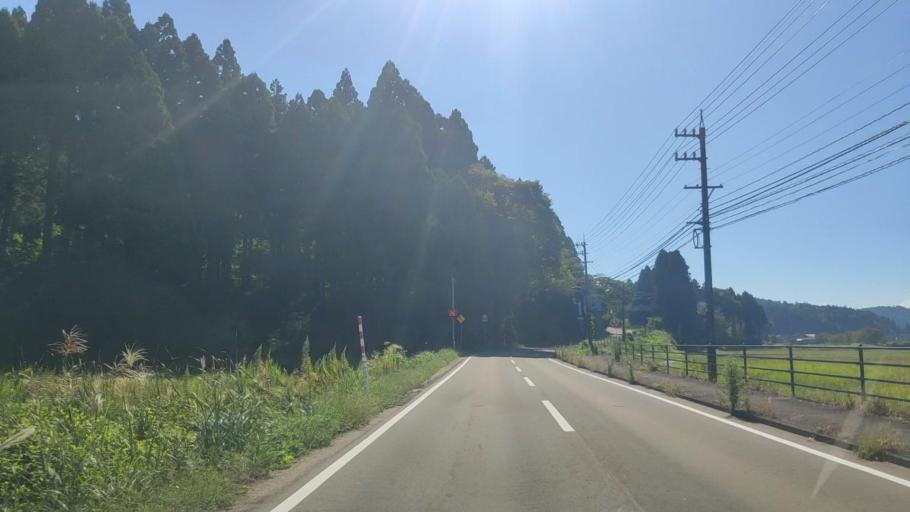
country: JP
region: Ishikawa
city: Nanao
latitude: 37.3501
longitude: 137.2341
